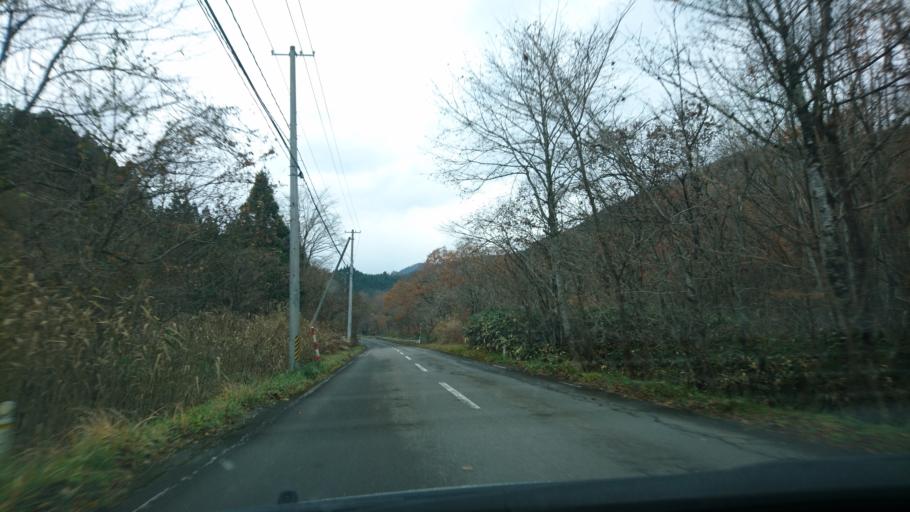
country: JP
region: Iwate
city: Ichinoseki
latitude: 38.9079
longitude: 140.8921
